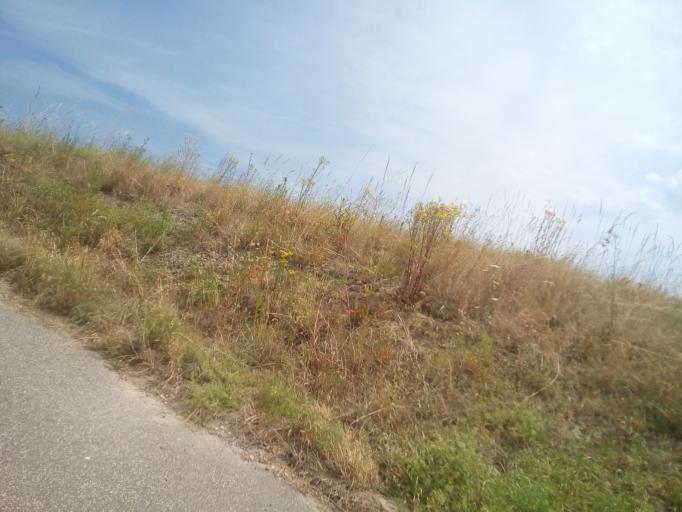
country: DE
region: Baden-Wuerttemberg
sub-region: Freiburg Region
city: Achern
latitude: 48.6471
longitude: 8.0234
